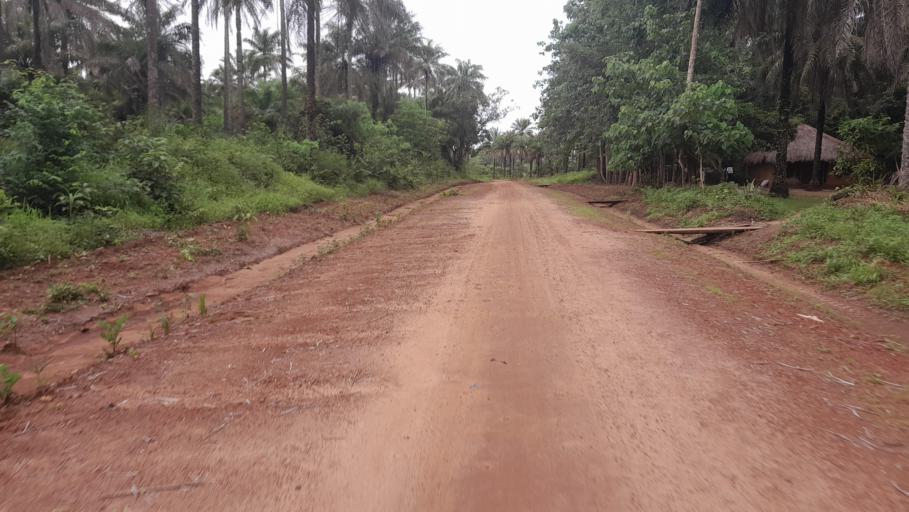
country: GN
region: Boke
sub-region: Boffa
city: Boffa
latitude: 10.0477
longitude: -13.8732
